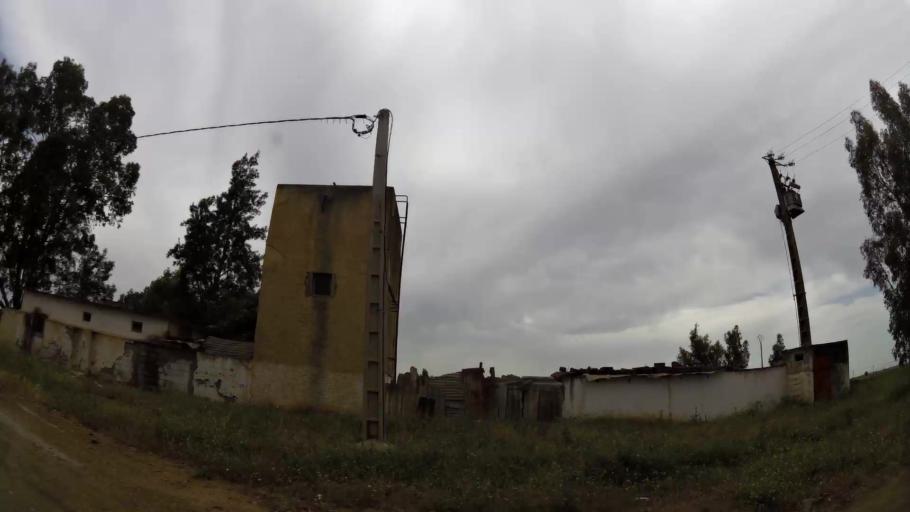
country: MA
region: Rabat-Sale-Zemmour-Zaer
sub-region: Khemisset
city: Tiflet
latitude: 33.8708
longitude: -6.2772
